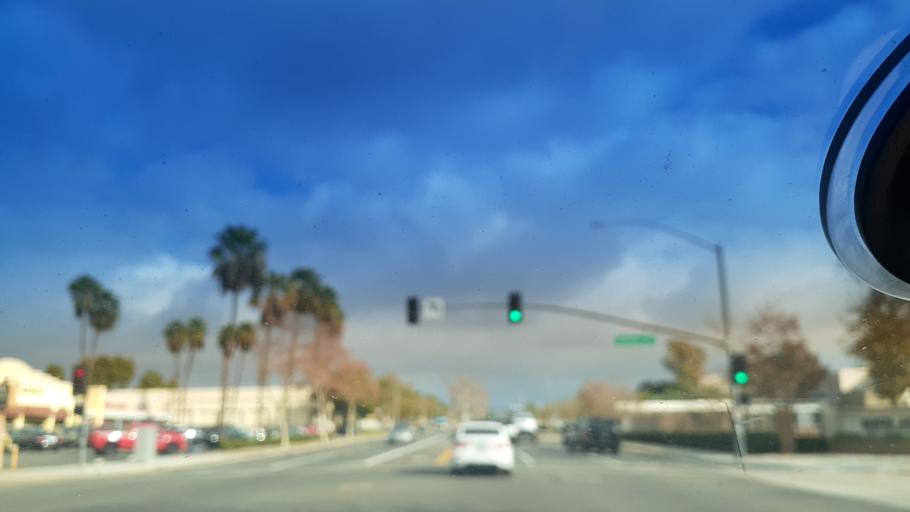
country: US
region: California
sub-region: Orange County
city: Santa Ana
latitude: 33.7600
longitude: -117.8917
